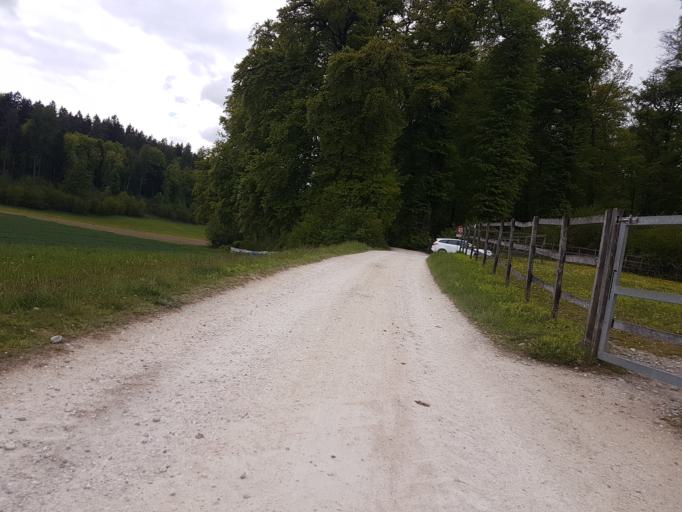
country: CH
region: Solothurn
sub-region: Bezirk Solothurn
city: Solothurn
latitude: 47.1951
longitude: 7.5295
